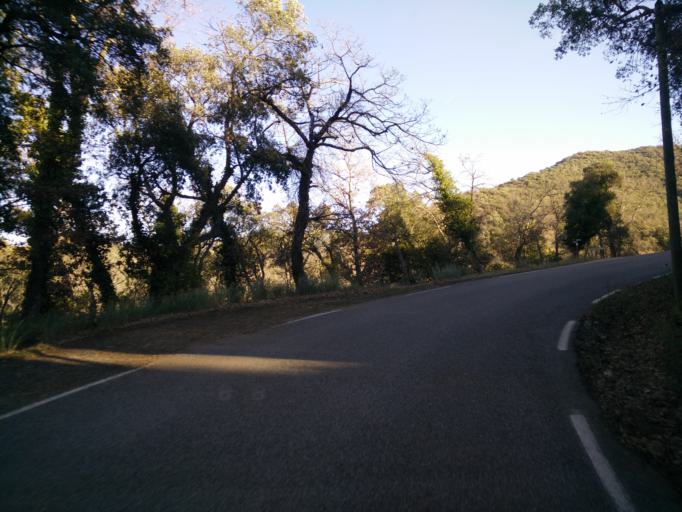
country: FR
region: Provence-Alpes-Cote d'Azur
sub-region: Departement du Var
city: Collobrieres
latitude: 43.2254
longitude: 6.2968
